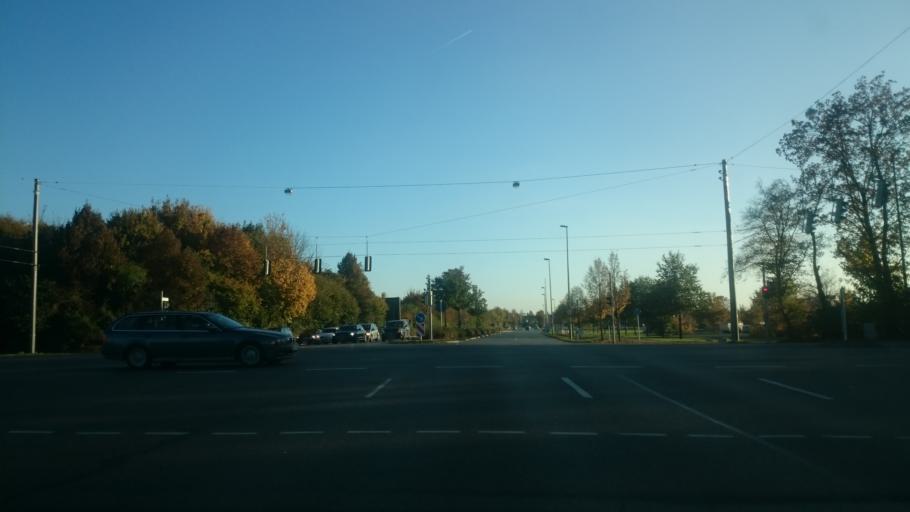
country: DE
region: Bavaria
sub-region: Swabia
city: Friedberg
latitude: 48.3561
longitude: 10.9654
